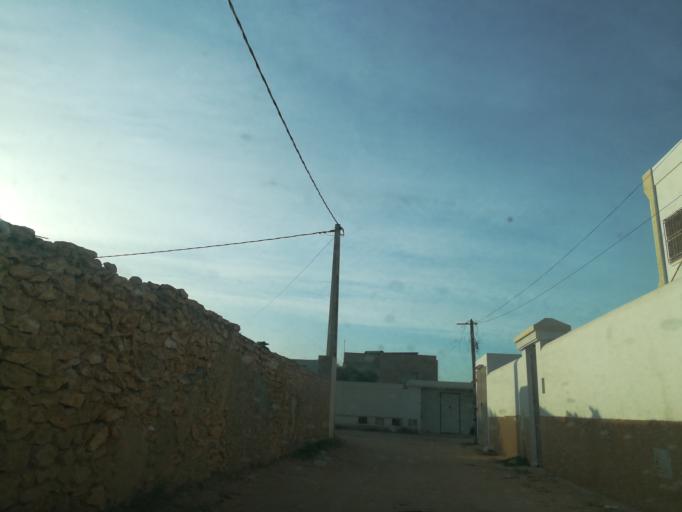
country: TN
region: Safaqis
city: Al Qarmadah
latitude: 34.8217
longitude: 10.7591
